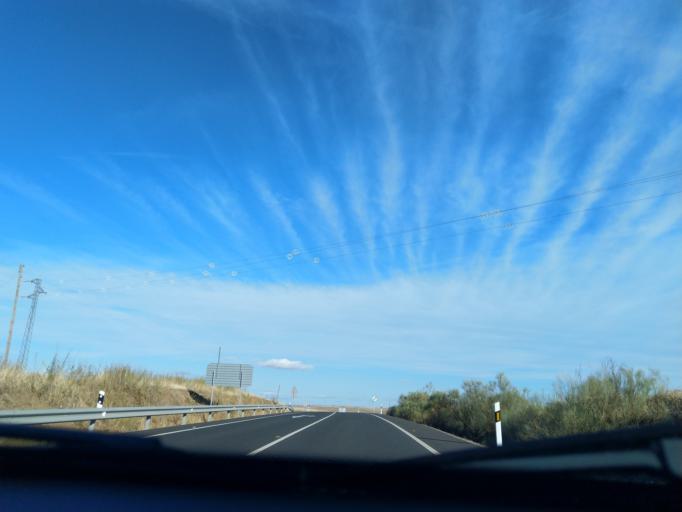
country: ES
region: Extremadura
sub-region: Provincia de Badajoz
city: Ahillones
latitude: 38.2639
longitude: -5.8602
